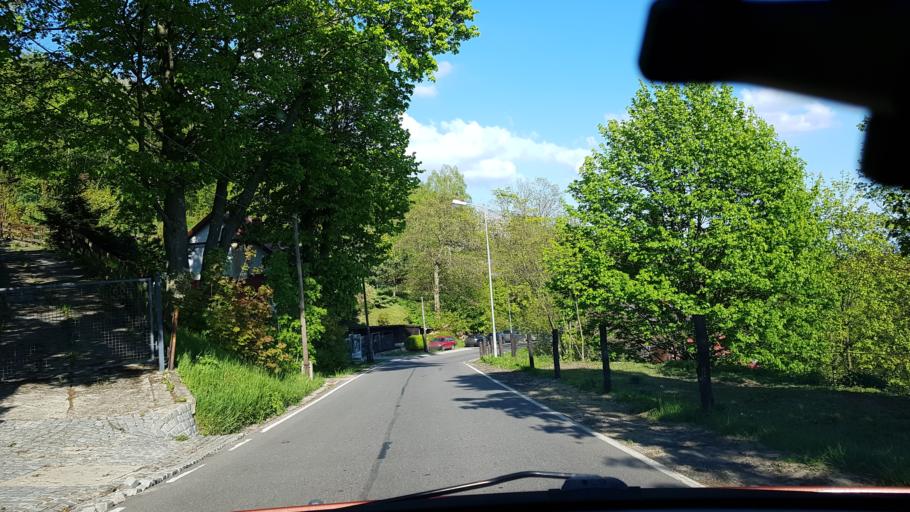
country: PL
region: Lower Silesian Voivodeship
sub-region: Powiat zabkowicki
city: Budzow
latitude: 50.5713
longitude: 16.6400
